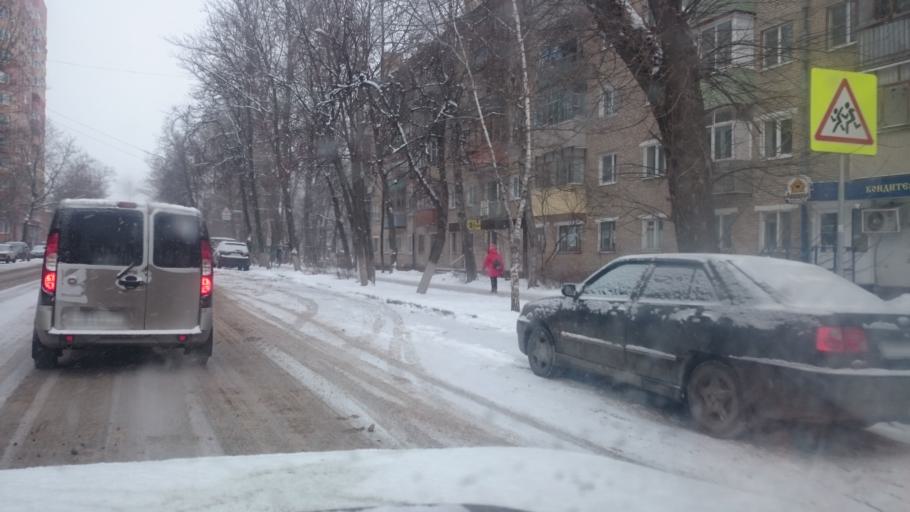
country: RU
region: Tula
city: Mendeleyevskiy
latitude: 54.1623
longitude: 37.5919
